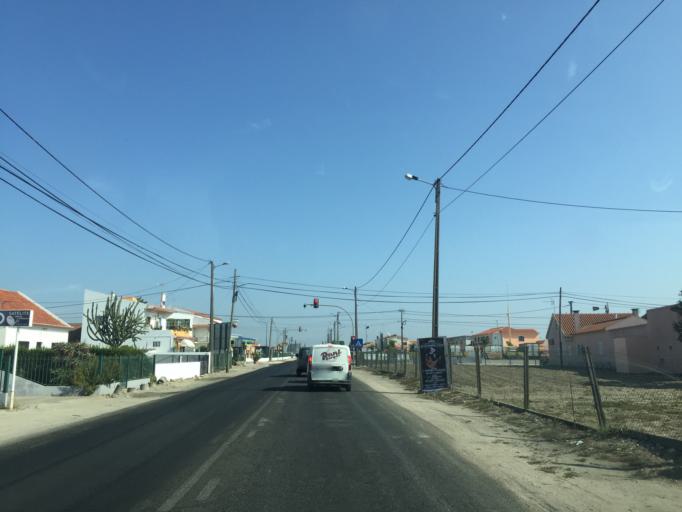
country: PT
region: Santarem
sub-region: Salvaterra de Magos
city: Marinhais
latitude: 39.0548
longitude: -8.7298
